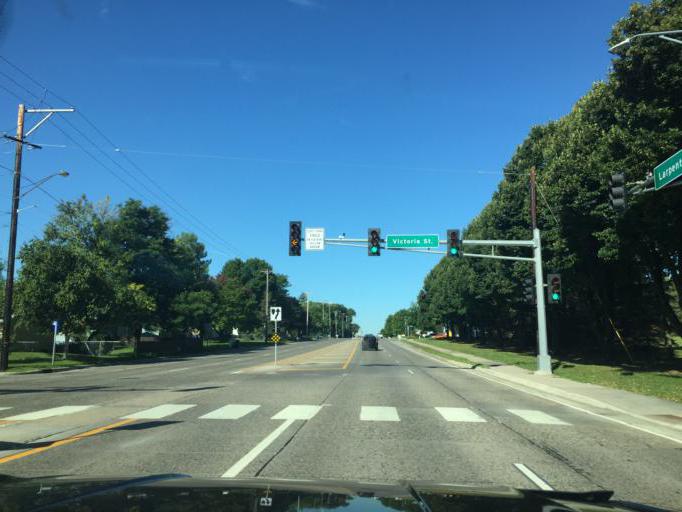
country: US
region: Minnesota
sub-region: Ramsey County
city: Roseville
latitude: 44.9920
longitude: -93.1375
